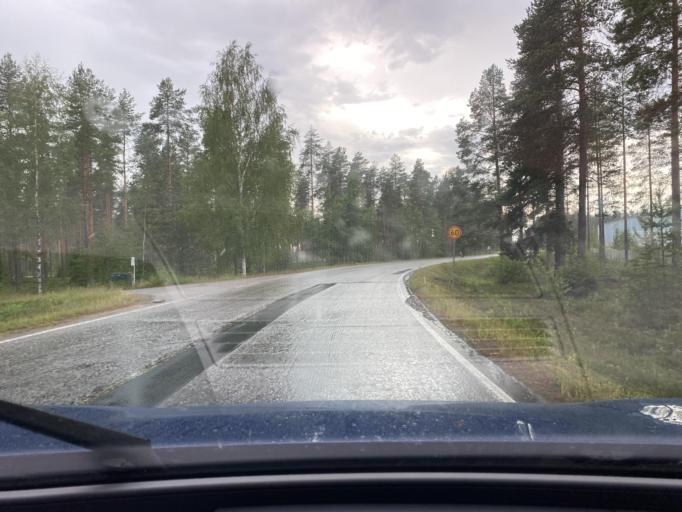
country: FI
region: Central Ostrobothnia
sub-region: Kaustinen
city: Veteli
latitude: 63.4681
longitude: 23.8287
